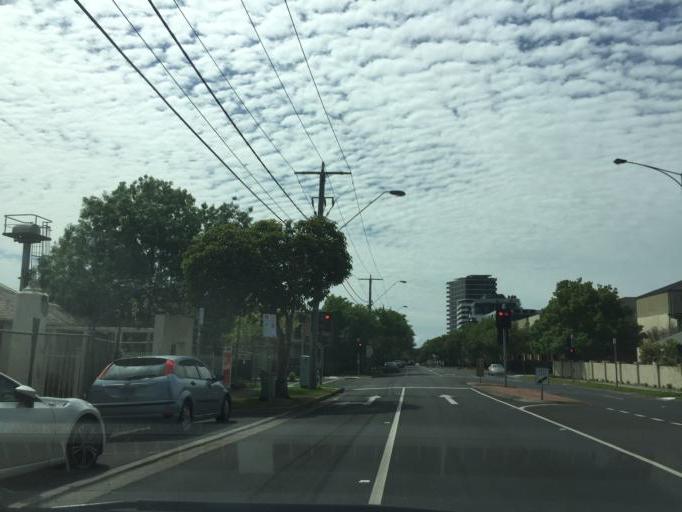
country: AU
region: Victoria
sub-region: Maribyrnong
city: Maribyrnong
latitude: -37.7733
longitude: 144.8814
